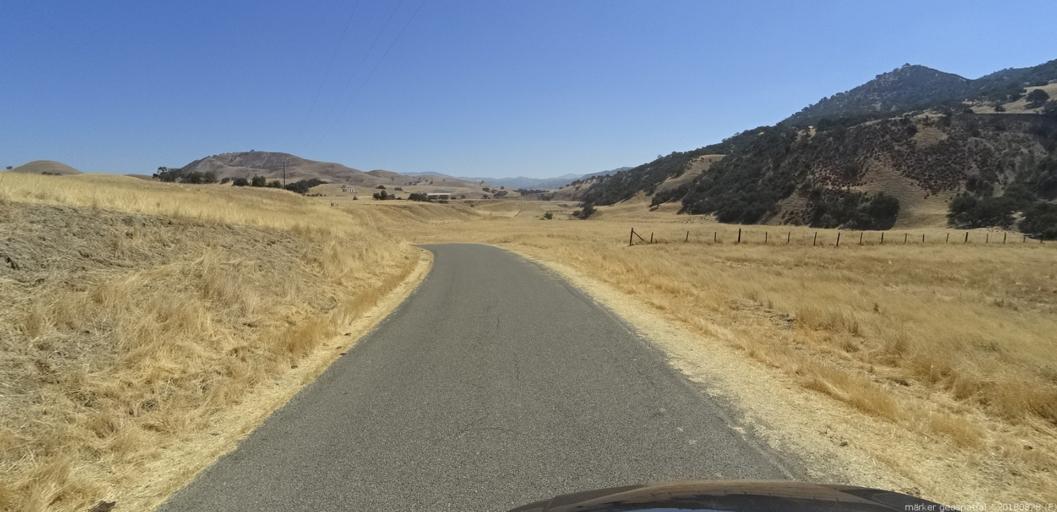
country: US
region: California
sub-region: San Luis Obispo County
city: San Miguel
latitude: 36.0644
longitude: -120.7891
